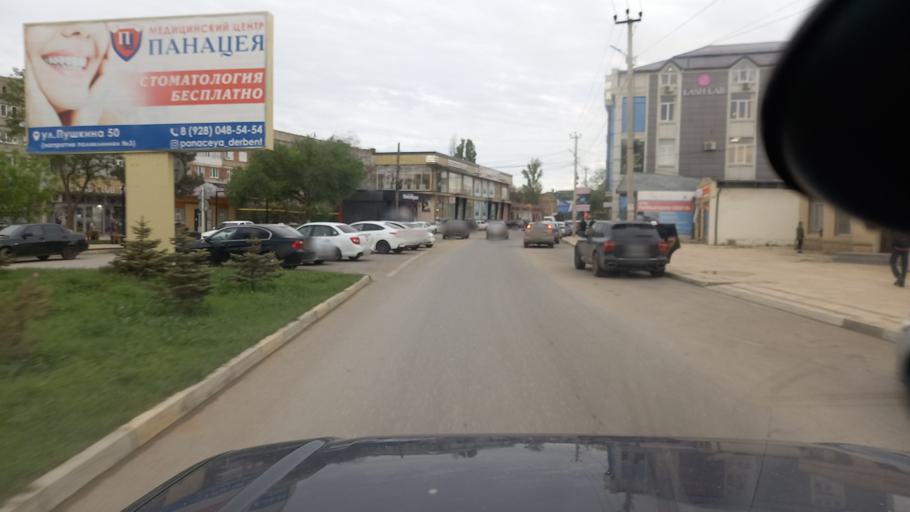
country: RU
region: Dagestan
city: Derbent
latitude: 42.0695
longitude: 48.2953
